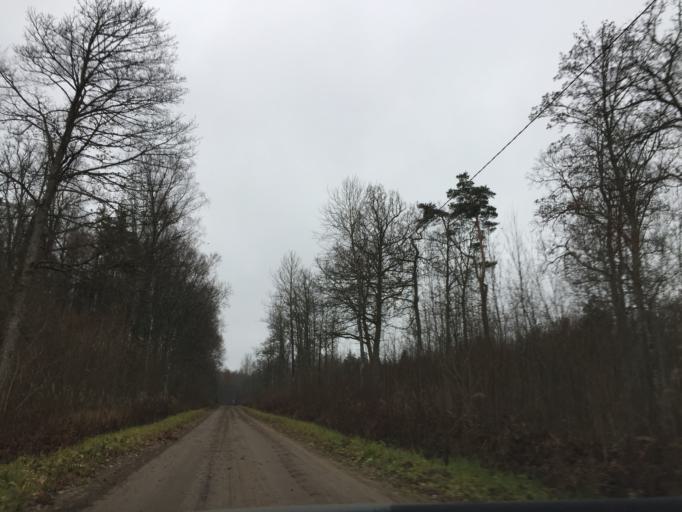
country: LV
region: Limbazu Rajons
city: Limbazi
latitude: 57.4978
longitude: 24.7704
